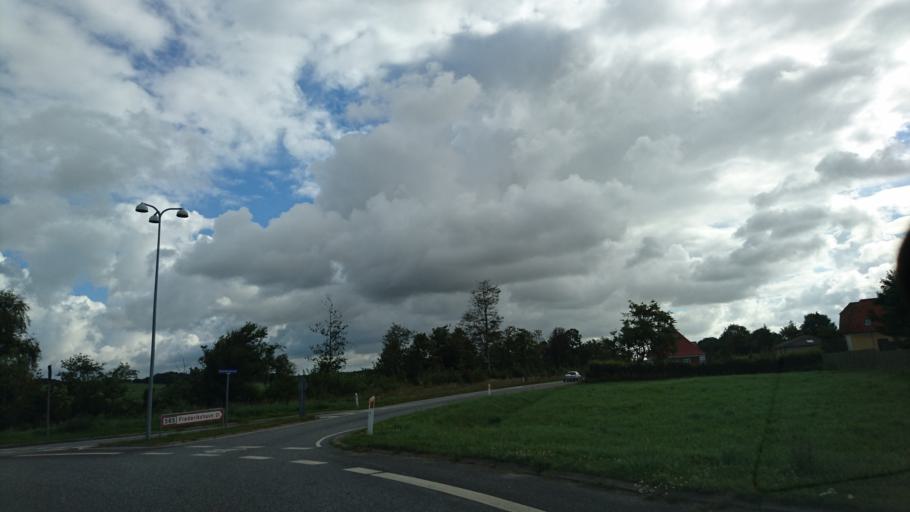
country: DK
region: North Denmark
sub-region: Hjorring Kommune
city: Tars
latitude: 57.3447
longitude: 10.2333
